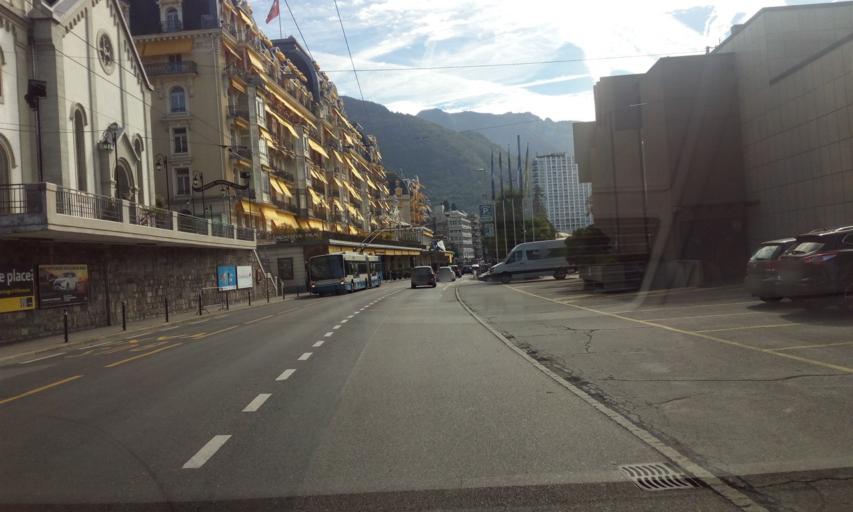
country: CH
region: Vaud
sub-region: Riviera-Pays-d'Enhaut District
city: Montreux
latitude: 46.4392
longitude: 6.9054
